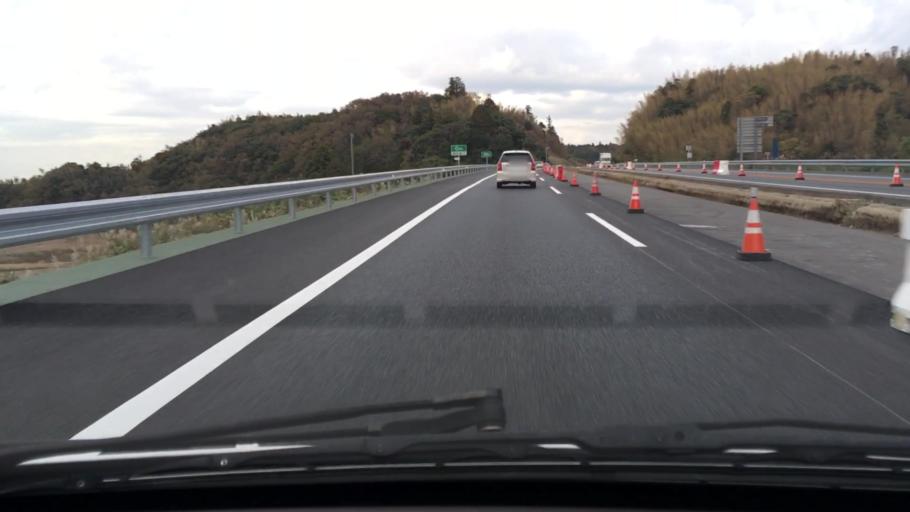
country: JP
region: Chiba
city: Kimitsu
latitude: 35.2885
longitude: 139.9288
